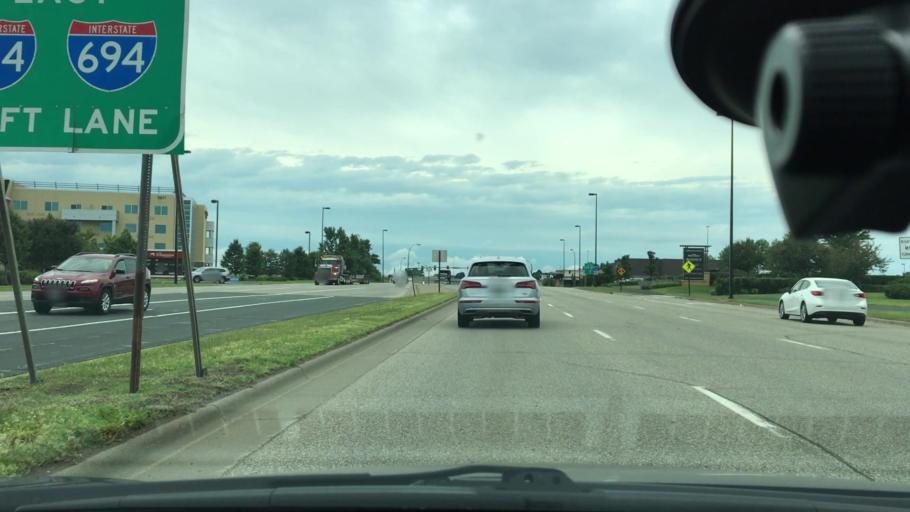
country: US
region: Minnesota
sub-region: Hennepin County
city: Maple Grove
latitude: 45.0936
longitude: -93.4317
